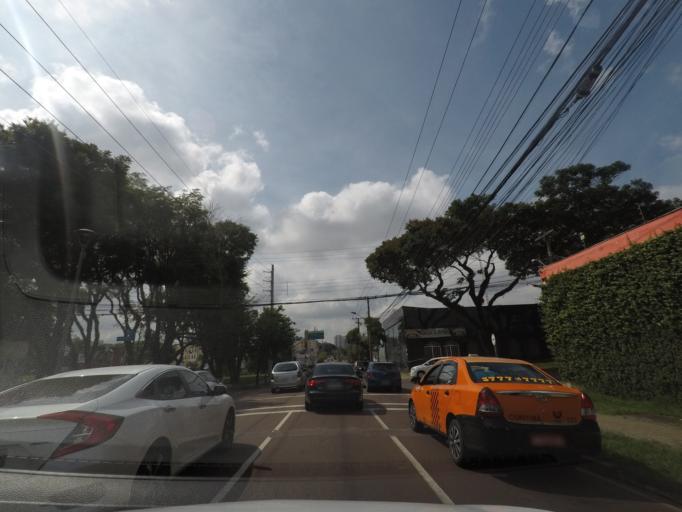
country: BR
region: Parana
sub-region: Curitiba
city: Curitiba
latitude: -25.4418
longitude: -49.2552
